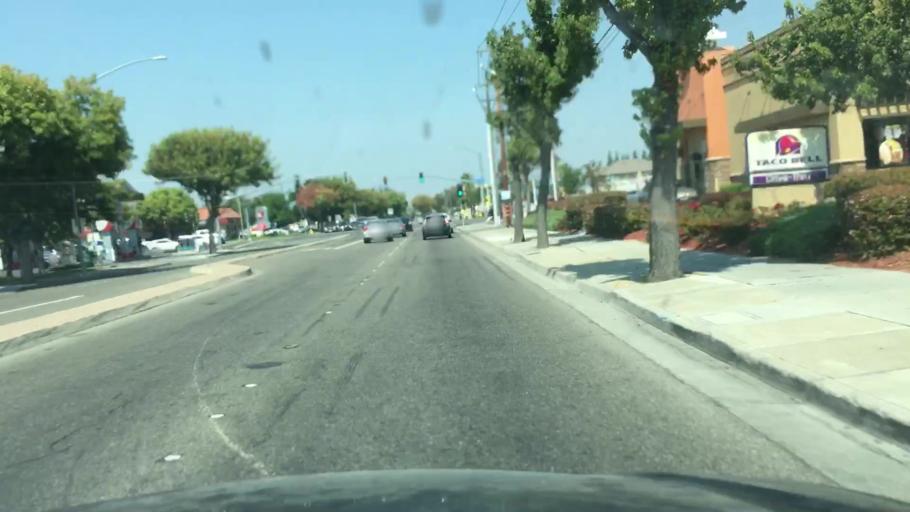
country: US
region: California
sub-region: San Joaquin County
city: Tracy
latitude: 37.7532
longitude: -121.4350
